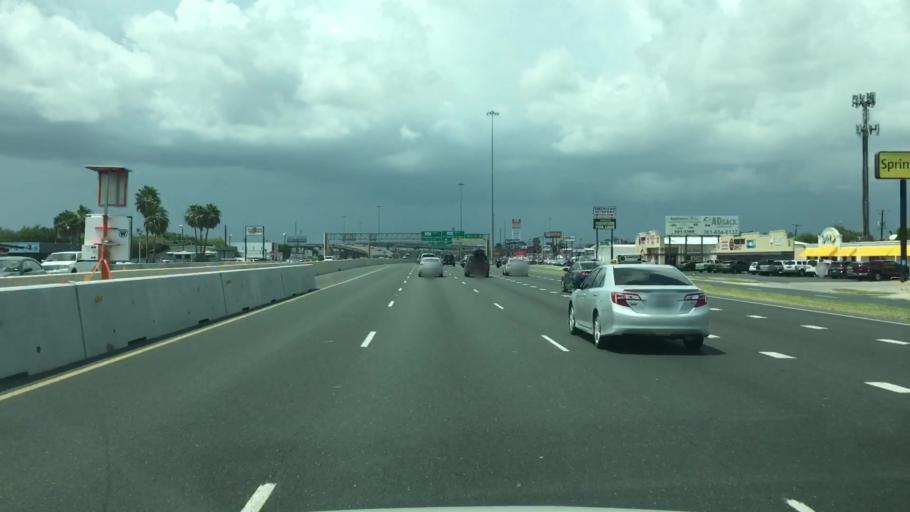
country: US
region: Texas
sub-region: Nueces County
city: Corpus Christi
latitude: 27.7326
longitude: -97.4211
